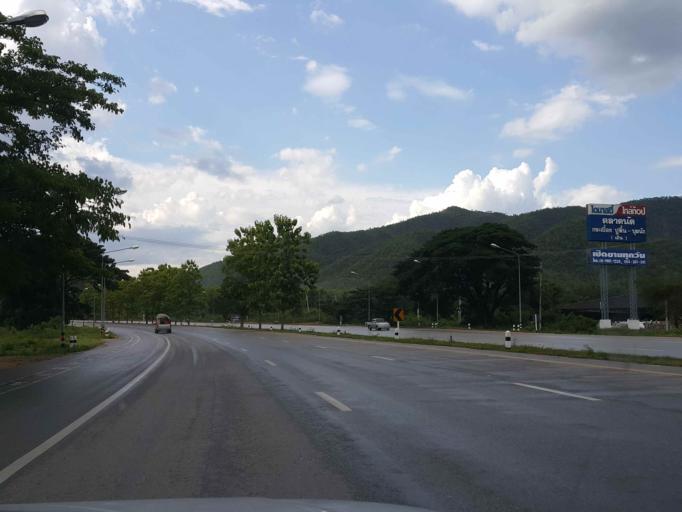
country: TH
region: Lampang
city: Thoen
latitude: 17.6551
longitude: 99.2509
